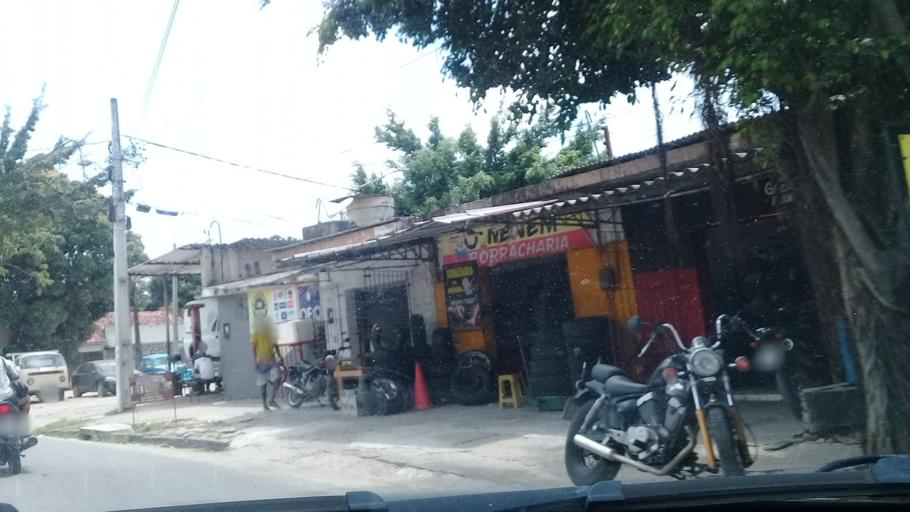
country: BR
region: Pernambuco
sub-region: Recife
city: Recife
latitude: -8.1072
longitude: -34.9222
